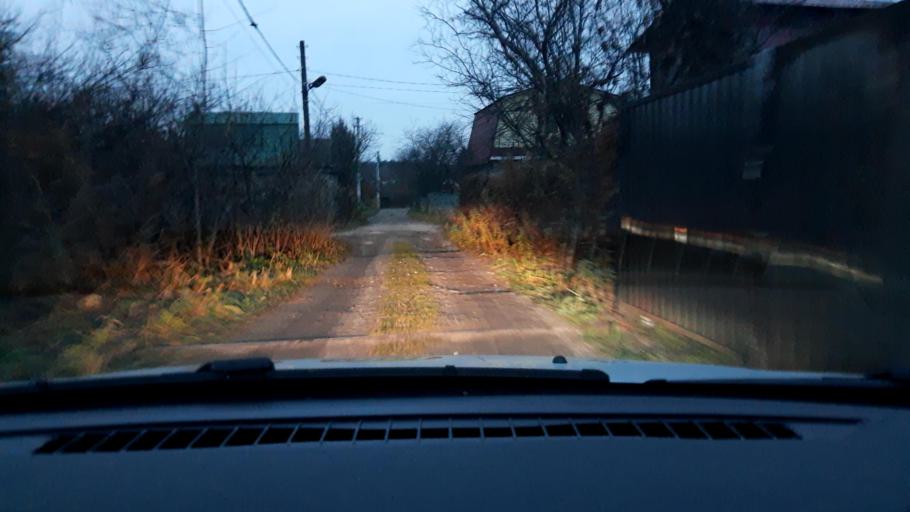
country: RU
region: Nizjnij Novgorod
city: Neklyudovo
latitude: 56.4298
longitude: 44.0092
